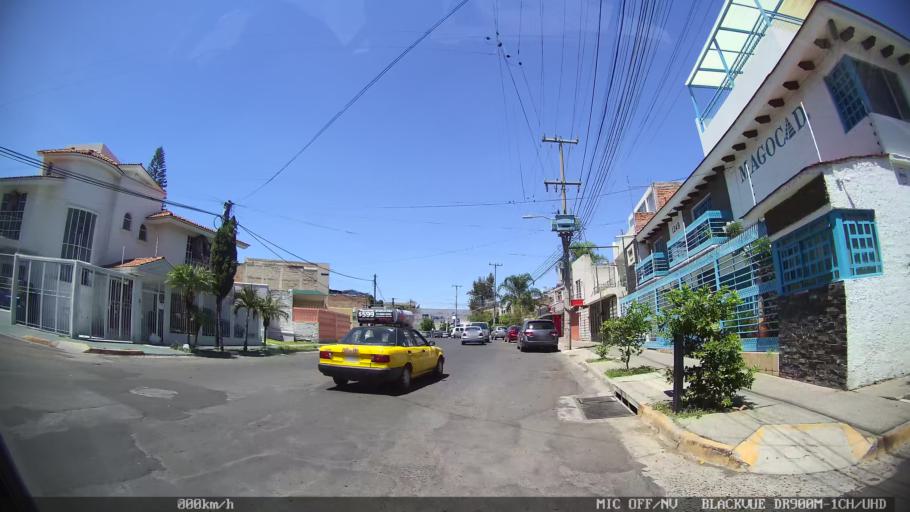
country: MX
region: Jalisco
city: Tlaquepaque
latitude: 20.6806
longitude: -103.2902
